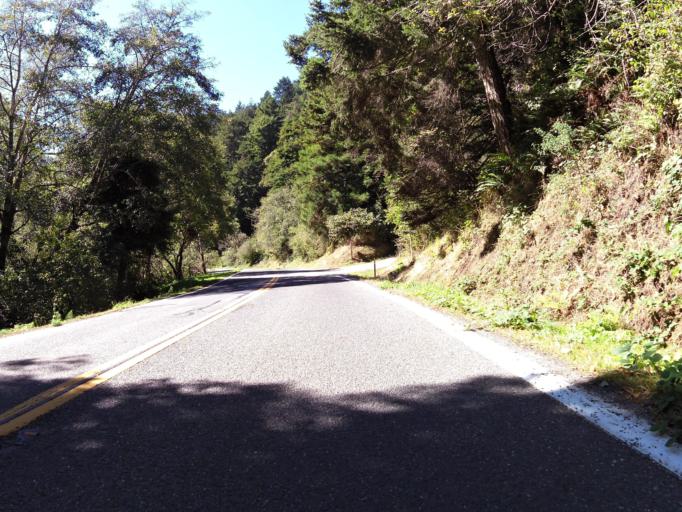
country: US
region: California
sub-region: Mendocino County
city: Fort Bragg
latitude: 39.7805
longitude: -123.8311
